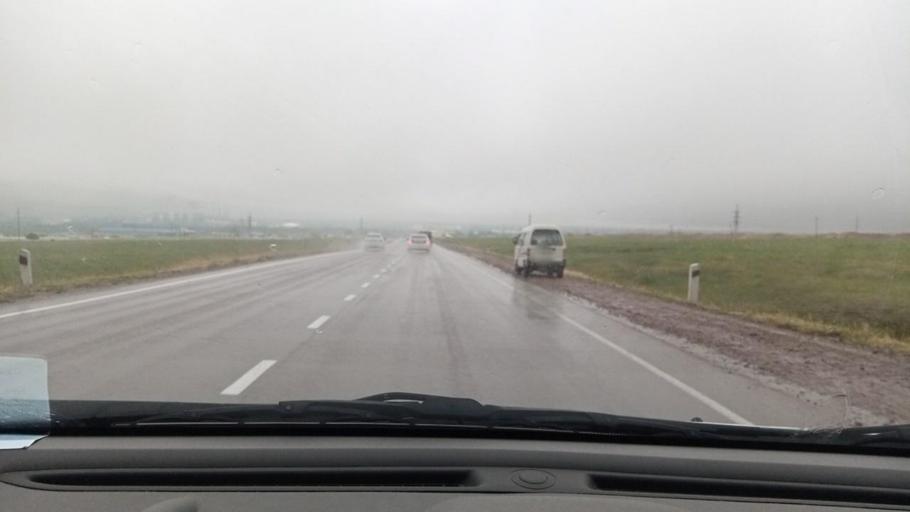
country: UZ
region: Toshkent
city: Angren
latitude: 41.0402
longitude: 70.1465
